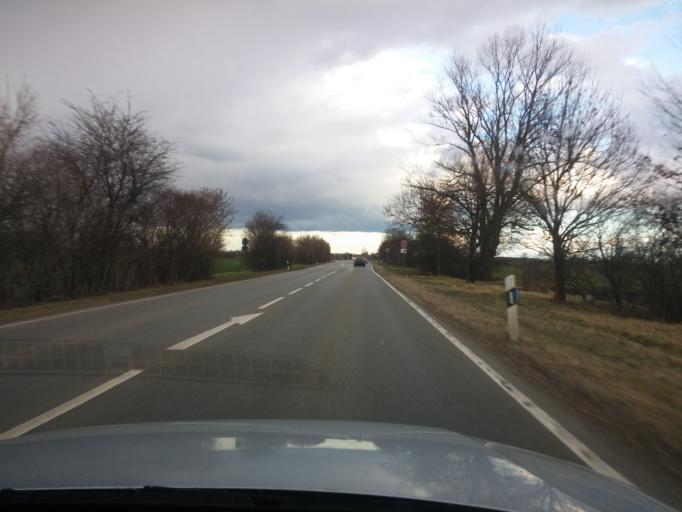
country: DE
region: Bavaria
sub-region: Upper Bavaria
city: Unterfoehring
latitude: 48.1826
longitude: 11.6685
